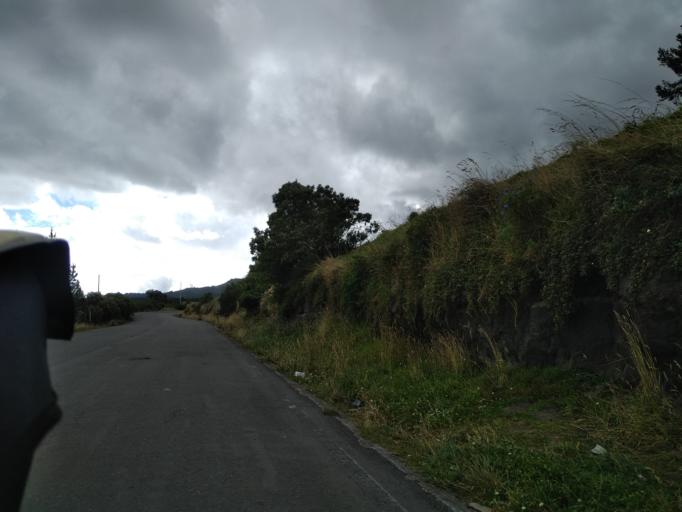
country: EC
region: Cotopaxi
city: Saquisili
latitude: -0.7196
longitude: -78.7623
